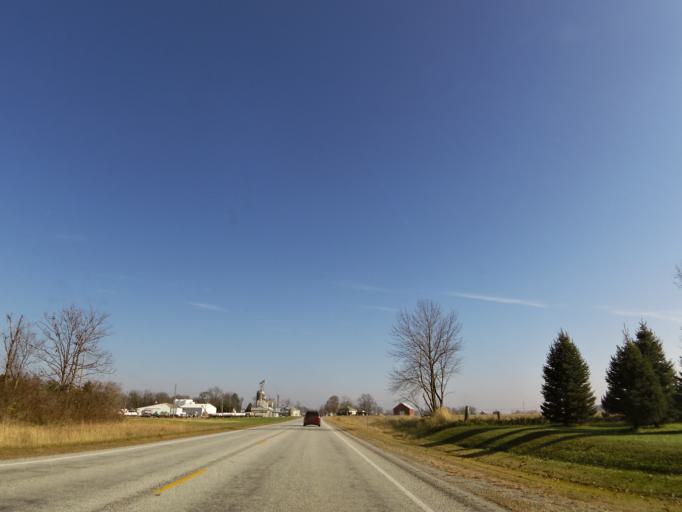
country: US
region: Indiana
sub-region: Shelby County
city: Shelbyville
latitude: 39.5530
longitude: -85.6733
